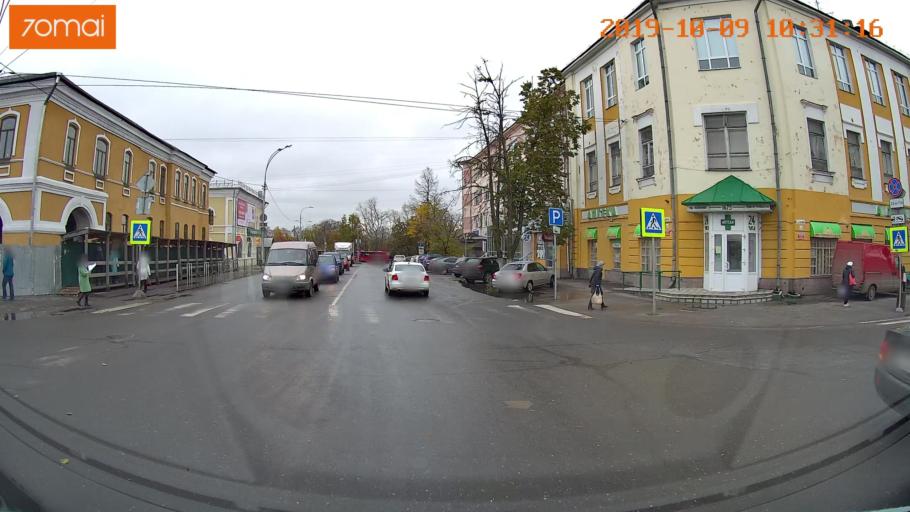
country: RU
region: Vologda
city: Vologda
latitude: 59.2213
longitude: 39.8932
